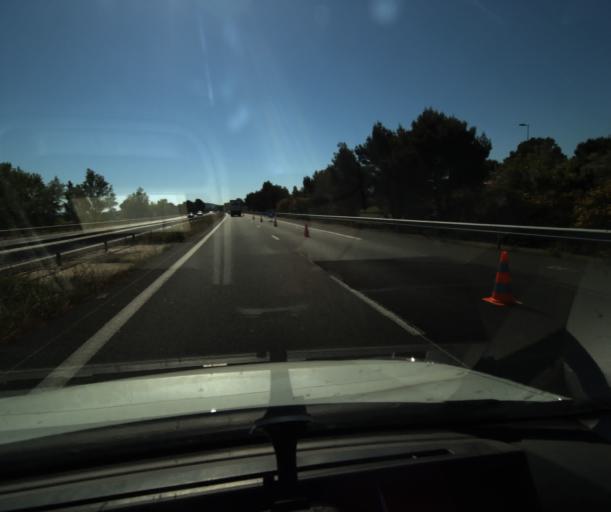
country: FR
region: Languedoc-Roussillon
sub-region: Departement de l'Aude
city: Fabrezan
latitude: 43.1702
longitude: 2.7026
